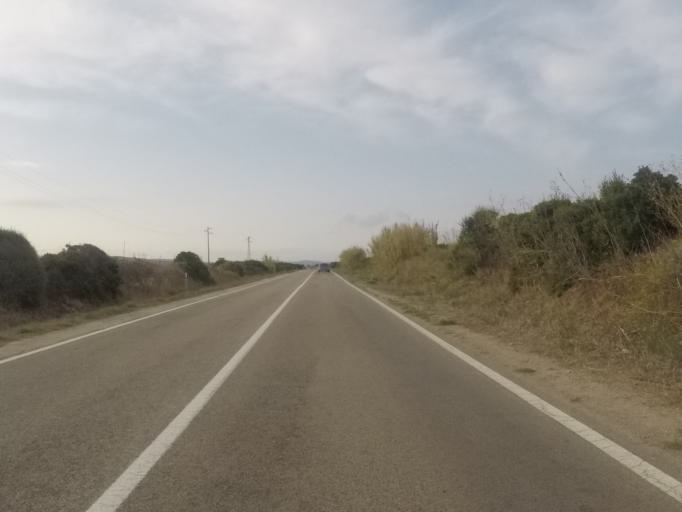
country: IT
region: Sardinia
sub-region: Provincia di Olbia-Tempio
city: Santa Teresa Gallura
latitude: 41.2144
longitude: 9.1838
